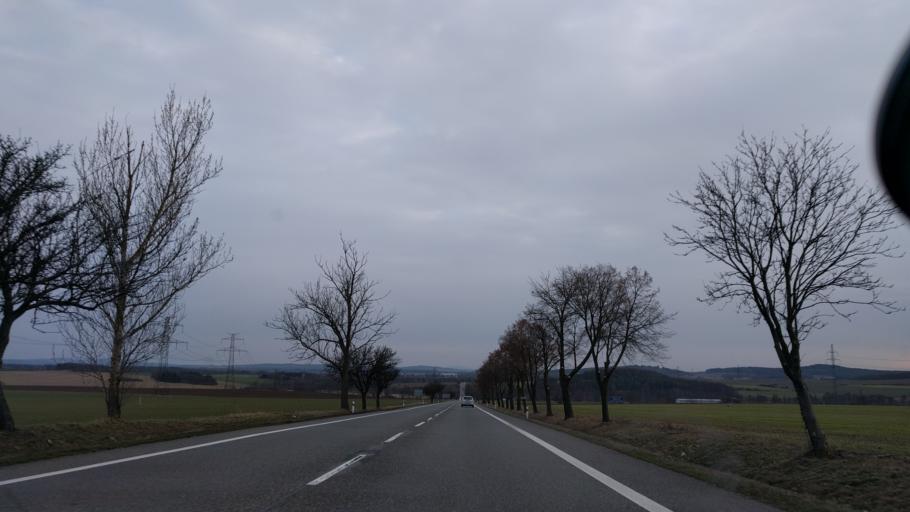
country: CZ
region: Jihocesky
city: Mirovice
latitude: 49.5070
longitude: 14.0744
